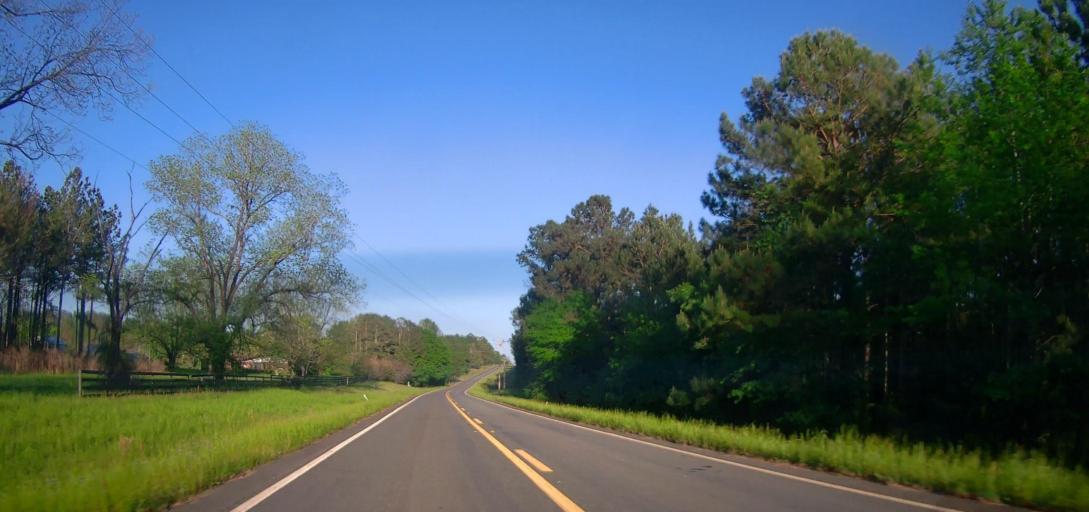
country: US
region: Georgia
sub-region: Macon County
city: Oglethorpe
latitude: 32.3199
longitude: -84.1957
